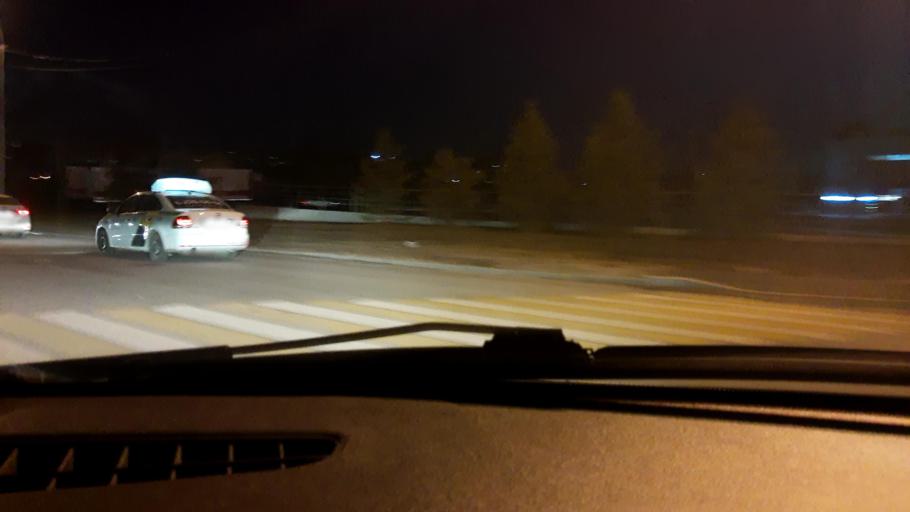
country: RU
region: Bashkortostan
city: Mikhaylovka
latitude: 54.7047
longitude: 55.8449
